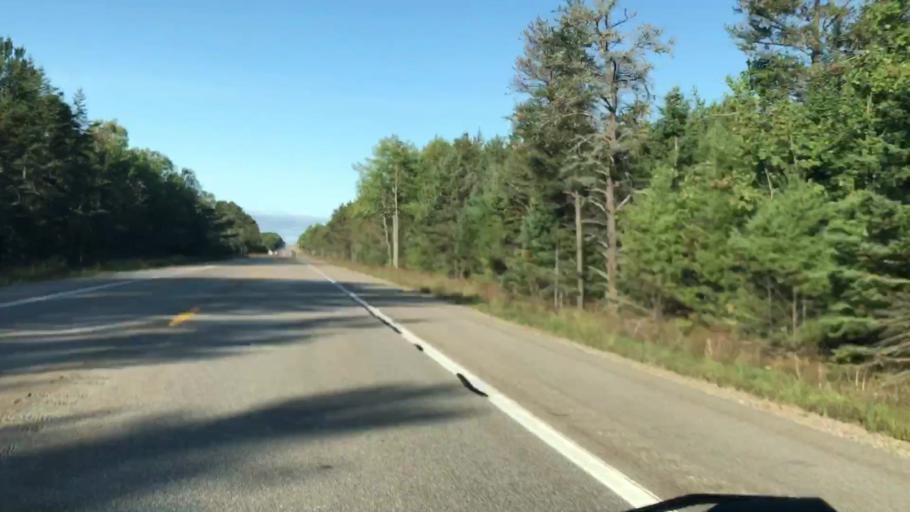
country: US
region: Michigan
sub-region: Chippewa County
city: Sault Ste. Marie
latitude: 46.3680
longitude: -84.7460
